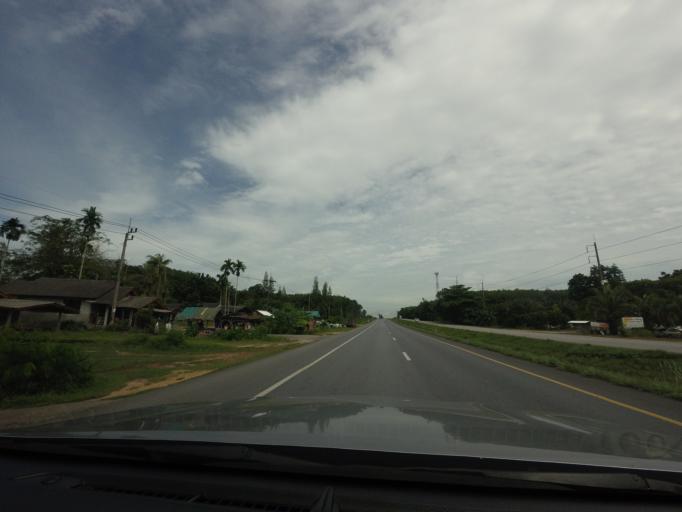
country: TH
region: Nakhon Si Thammarat
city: Thung Yai
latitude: 8.3240
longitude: 99.4531
